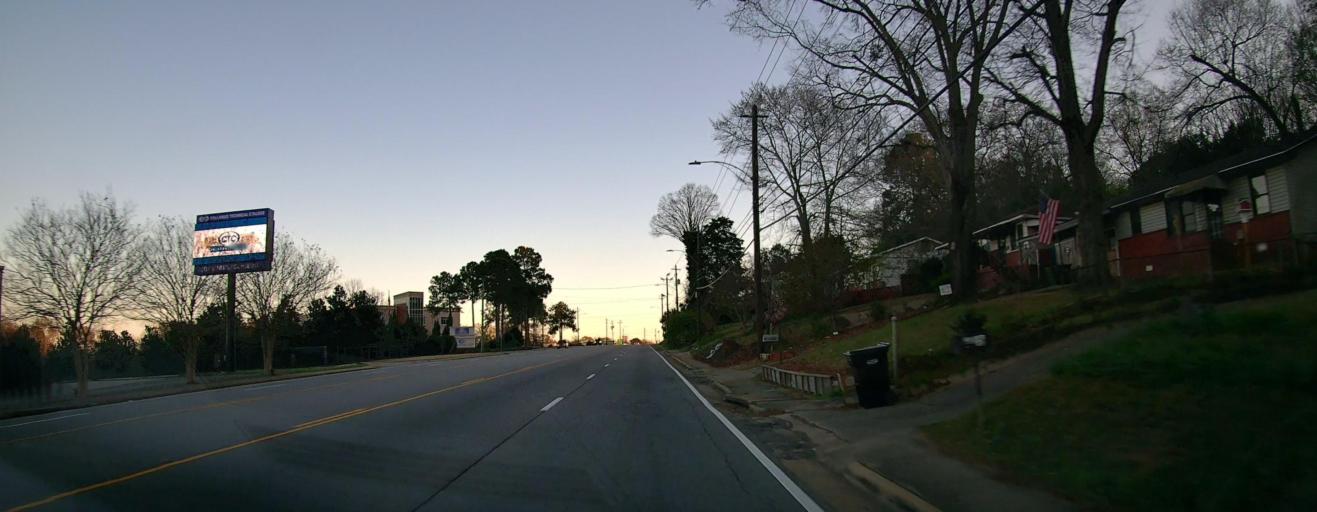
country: US
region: Alabama
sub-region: Russell County
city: Phenix City
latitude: 32.5107
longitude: -84.9796
